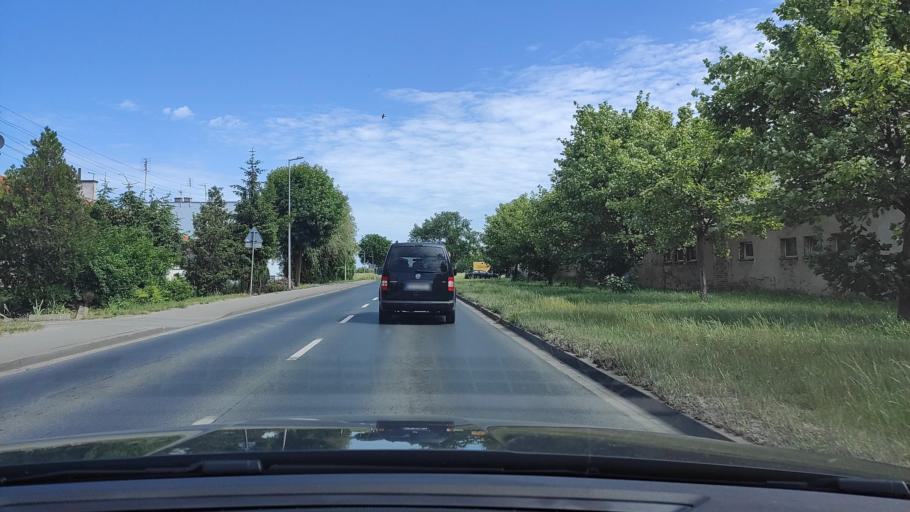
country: PL
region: Greater Poland Voivodeship
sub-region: Powiat poznanski
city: Czerwonak
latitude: 52.5182
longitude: 16.9748
